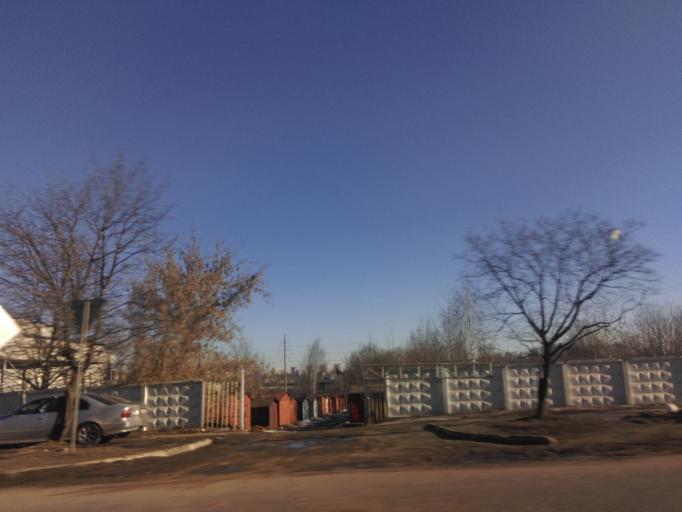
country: RU
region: Moskovskaya
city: Odintsovo
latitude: 55.6714
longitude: 37.3045
